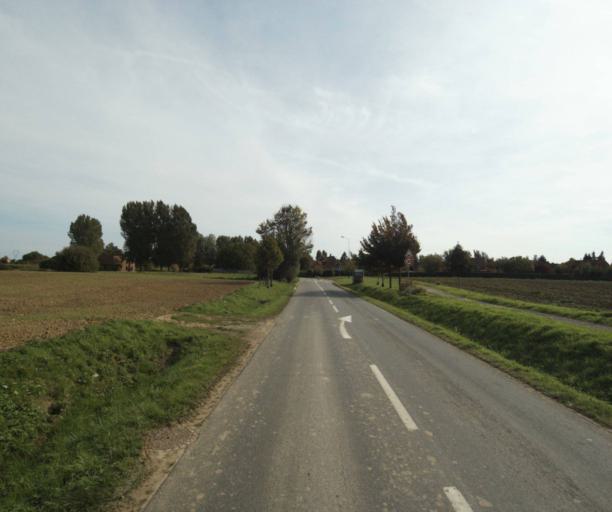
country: FR
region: Nord-Pas-de-Calais
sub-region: Departement du Nord
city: Radinghem-en-Weppes
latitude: 50.6088
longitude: 2.9111
